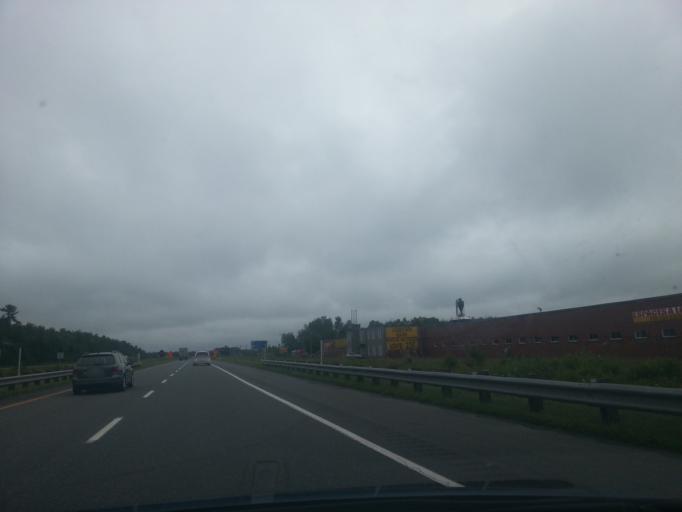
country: CA
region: Quebec
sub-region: Mauricie
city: Daveluyville
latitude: 46.2057
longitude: -72.0746
